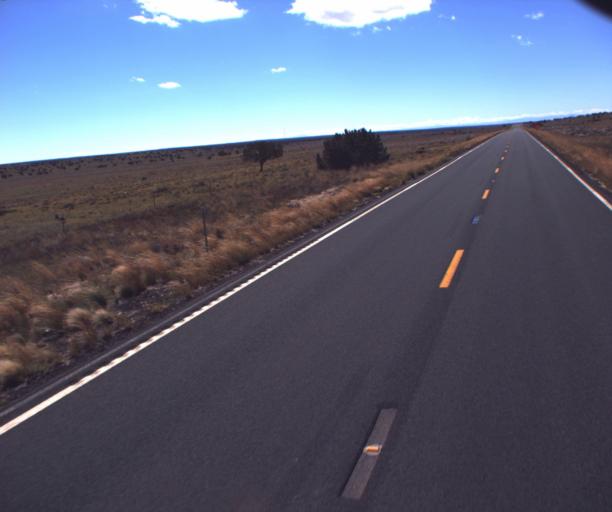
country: US
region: Arizona
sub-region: Apache County
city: Houck
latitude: 34.9518
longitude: -109.2311
